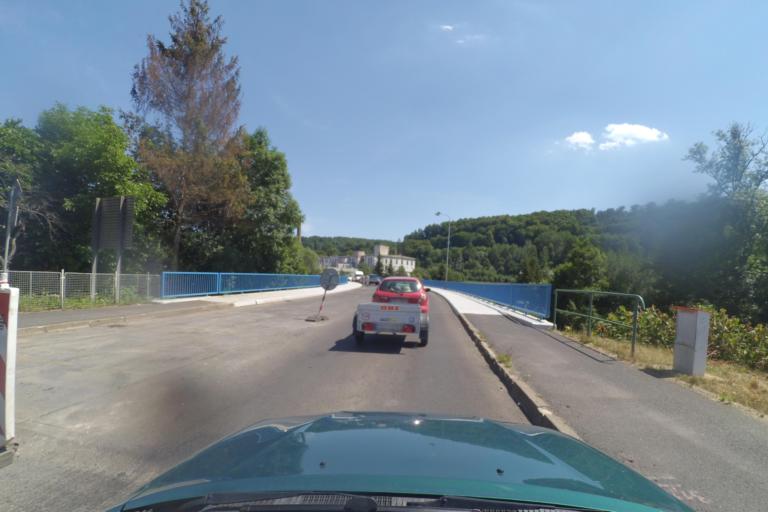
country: CZ
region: Ustecky
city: Benesov nad Ploucnici
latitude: 50.7407
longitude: 14.3038
